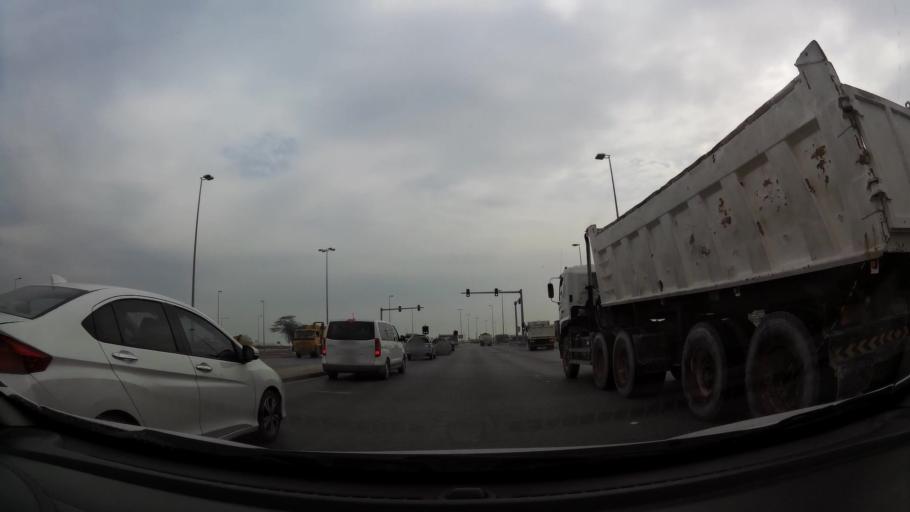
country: BH
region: Northern
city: Sitrah
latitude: 26.0749
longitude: 50.6145
